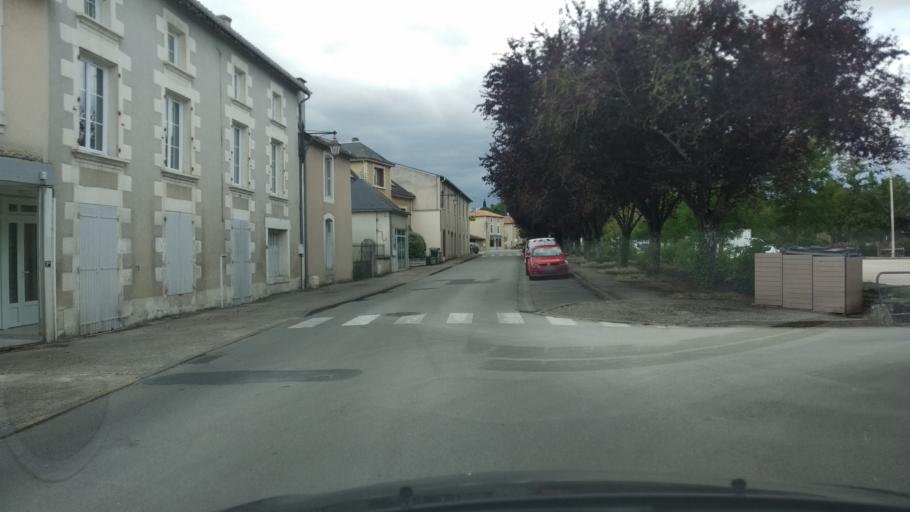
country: FR
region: Poitou-Charentes
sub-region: Departement de la Vienne
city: Vouille
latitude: 46.6378
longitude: 0.1660
